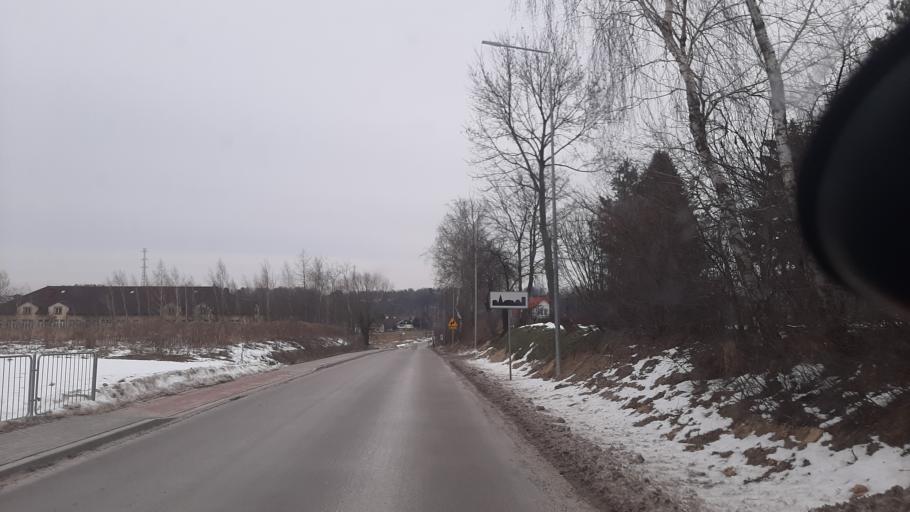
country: PL
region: Lublin Voivodeship
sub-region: Powiat lubelski
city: Jakubowice Murowane
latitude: 51.2982
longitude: 22.6323
